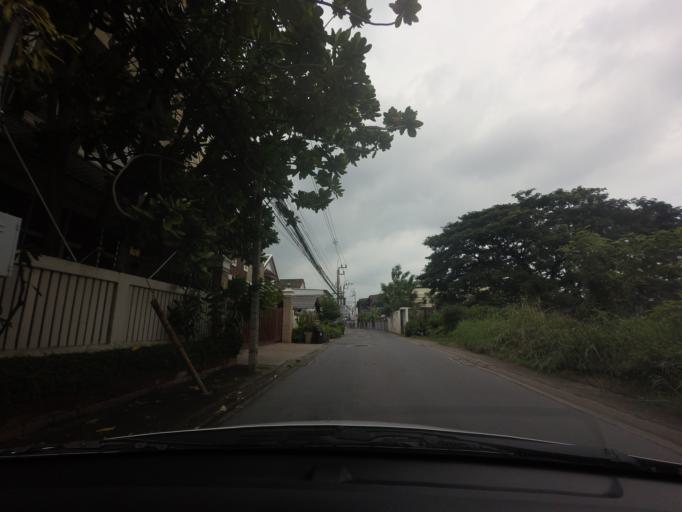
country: TH
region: Bangkok
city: Lak Si
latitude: 13.8952
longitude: 100.5647
